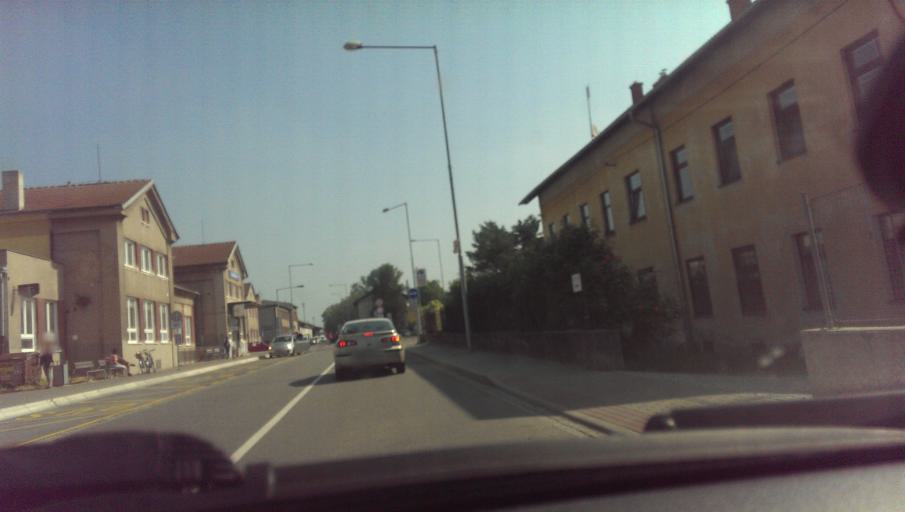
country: CZ
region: Zlin
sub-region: Okres Uherske Hradiste
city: Stare Mesto
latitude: 49.0756
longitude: 17.4229
